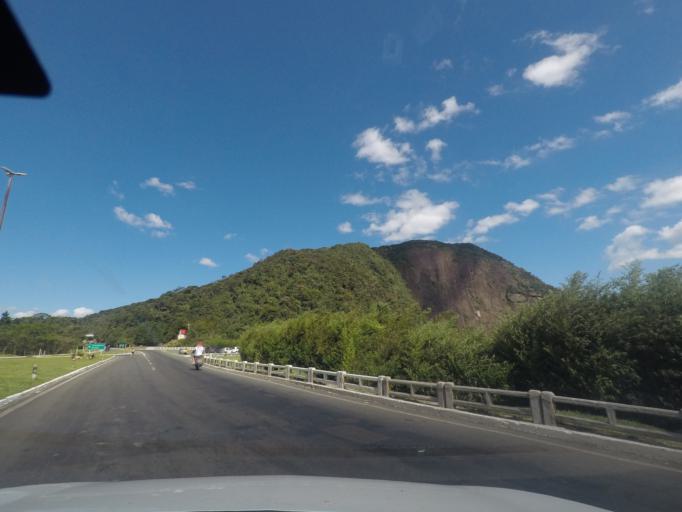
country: BR
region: Rio de Janeiro
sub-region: Teresopolis
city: Teresopolis
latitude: -22.4625
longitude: -42.9877
